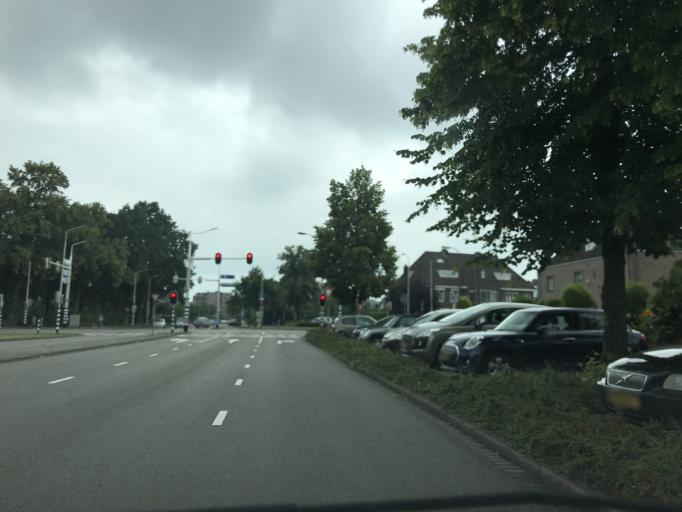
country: NL
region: North Brabant
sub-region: Gemeente Breda
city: Breda
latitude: 51.5780
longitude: 4.7705
